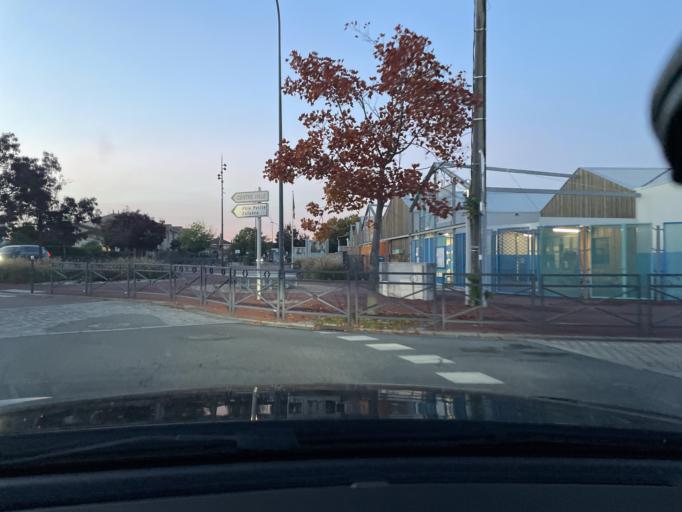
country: FR
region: Aquitaine
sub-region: Departement de la Gironde
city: Le Bouscat
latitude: 44.8799
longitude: -0.5910
